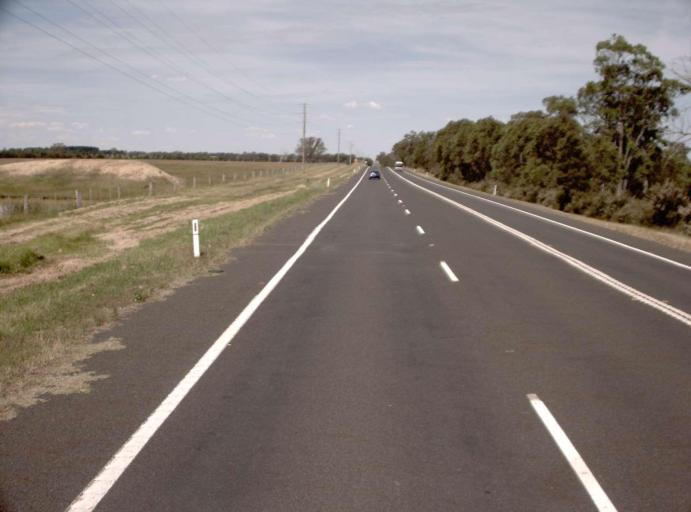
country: AU
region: Victoria
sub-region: East Gippsland
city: Bairnsdale
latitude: -37.8848
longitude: 147.4052
